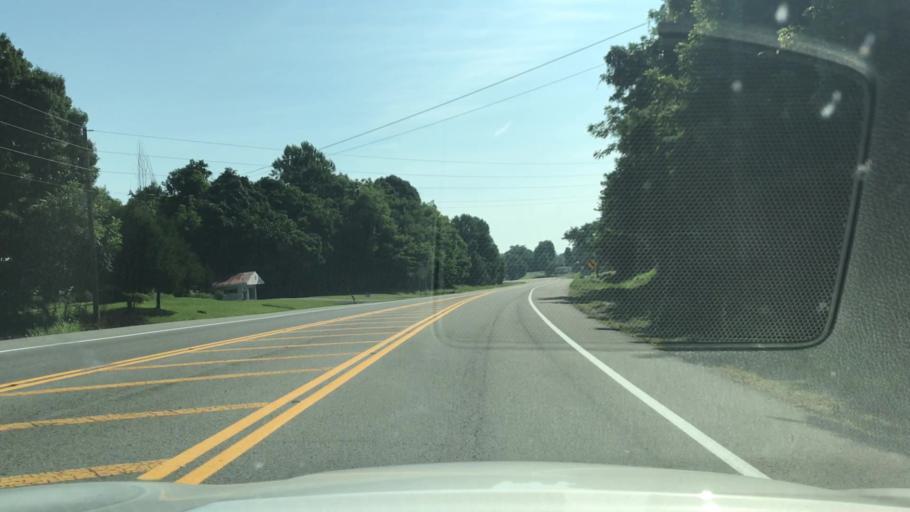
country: US
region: Tennessee
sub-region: Pickett County
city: Byrdstown
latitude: 36.5717
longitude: -85.1603
